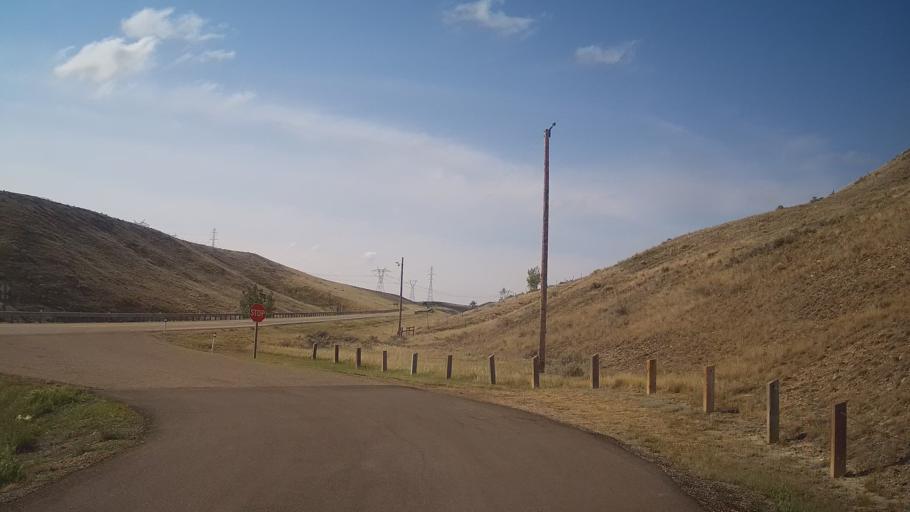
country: CA
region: Alberta
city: Brooks
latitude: 50.9135
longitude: -111.9003
